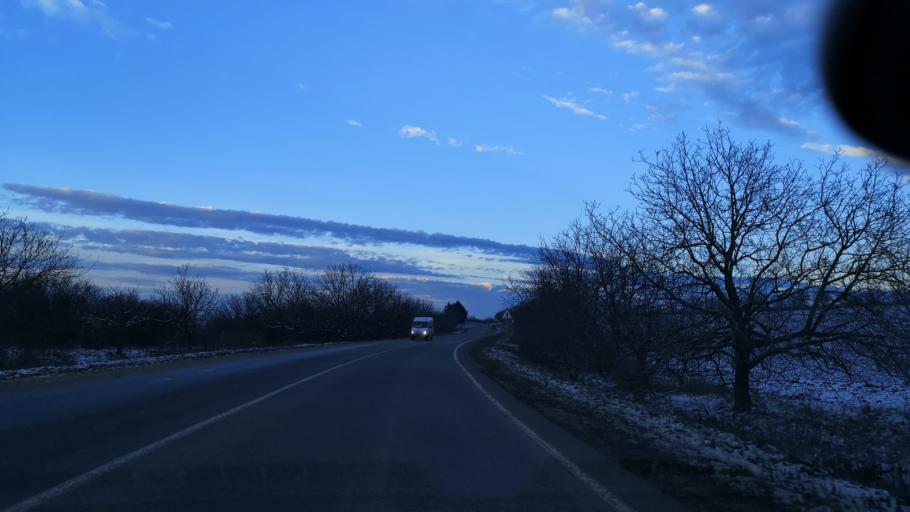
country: MD
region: Orhei
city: Orhei
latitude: 47.5490
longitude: 28.7928
